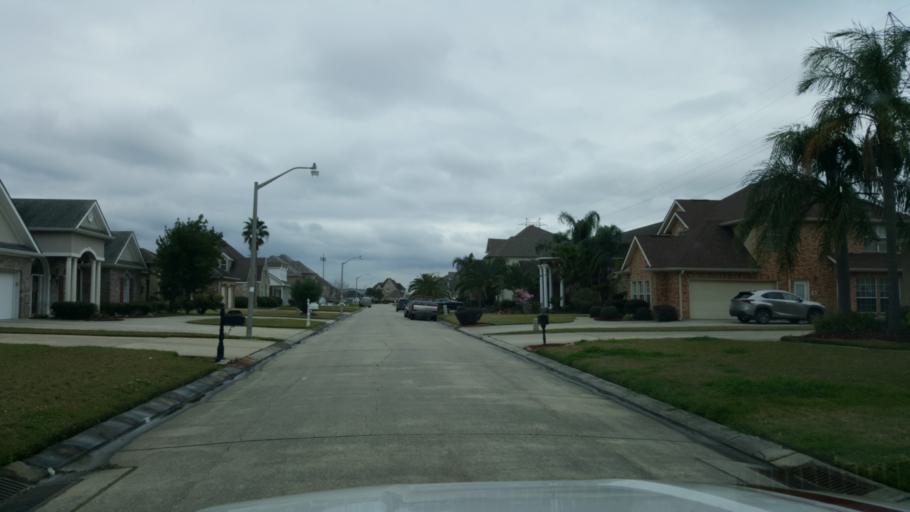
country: US
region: Louisiana
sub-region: Jefferson Parish
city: Harvey
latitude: 29.8808
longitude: -90.0795
